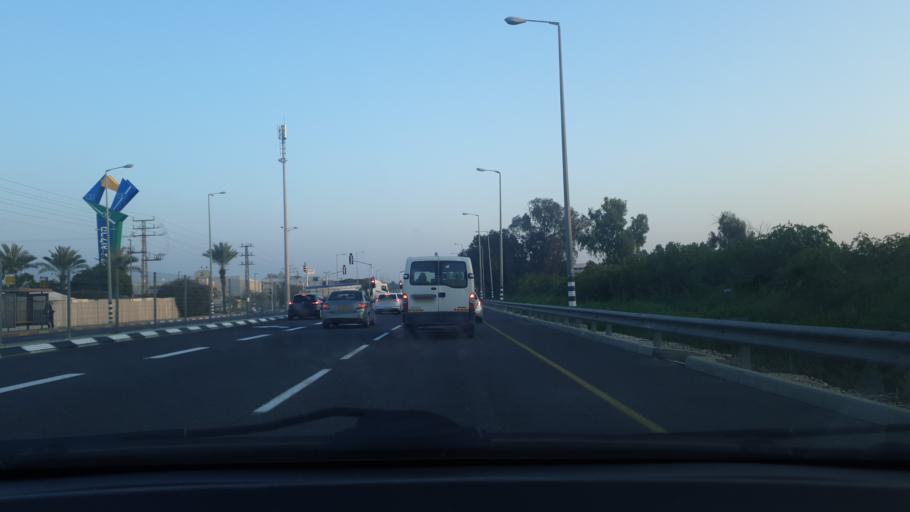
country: IL
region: Central District
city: Kefar Habad
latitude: 31.9645
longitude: 34.8479
